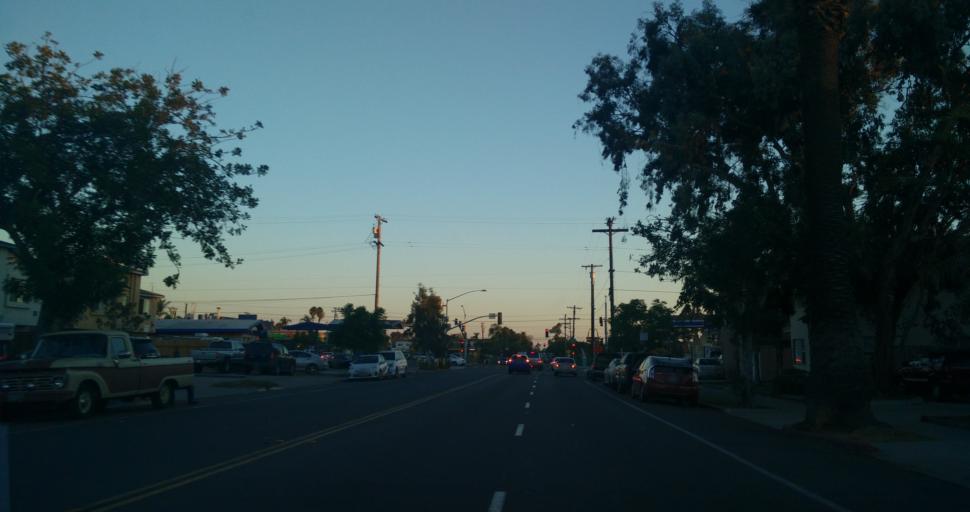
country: US
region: California
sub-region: San Diego County
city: San Diego
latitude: 32.7565
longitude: -117.1389
